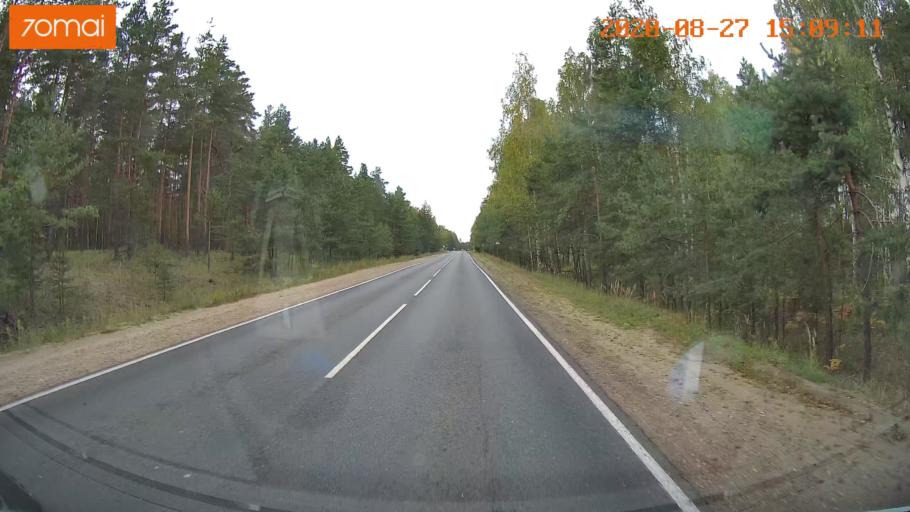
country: RU
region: Vladimir
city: Kurlovo
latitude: 55.5017
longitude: 40.5726
